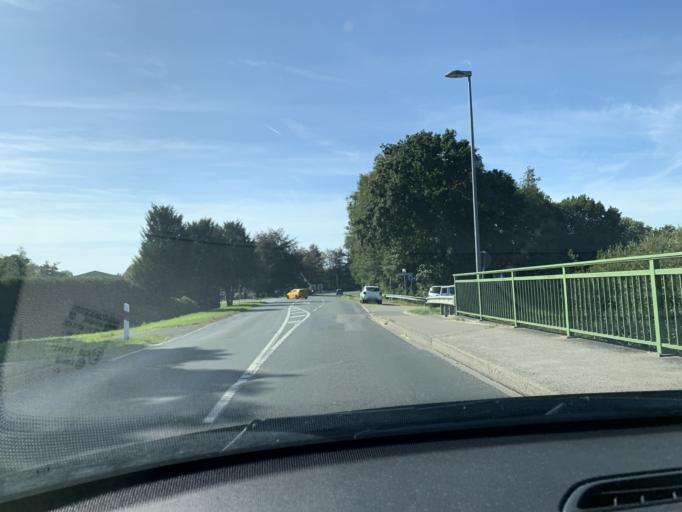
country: DE
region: Lower Saxony
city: Barssel
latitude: 53.1732
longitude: 7.7534
